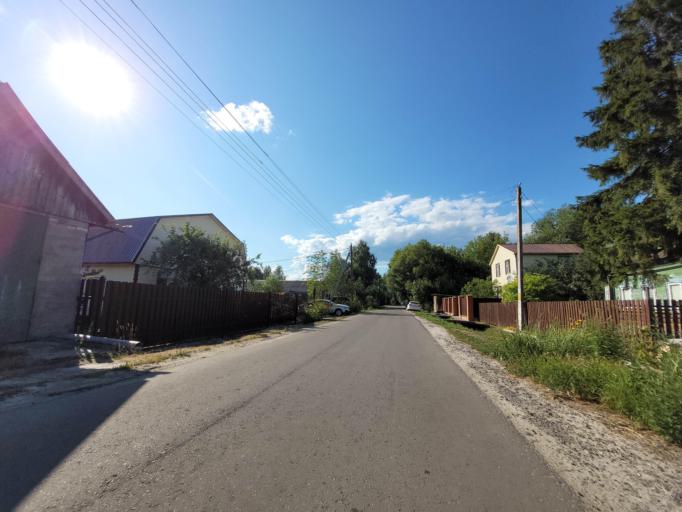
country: RU
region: Moskovskaya
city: Konobeyevo
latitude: 55.4103
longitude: 38.6985
